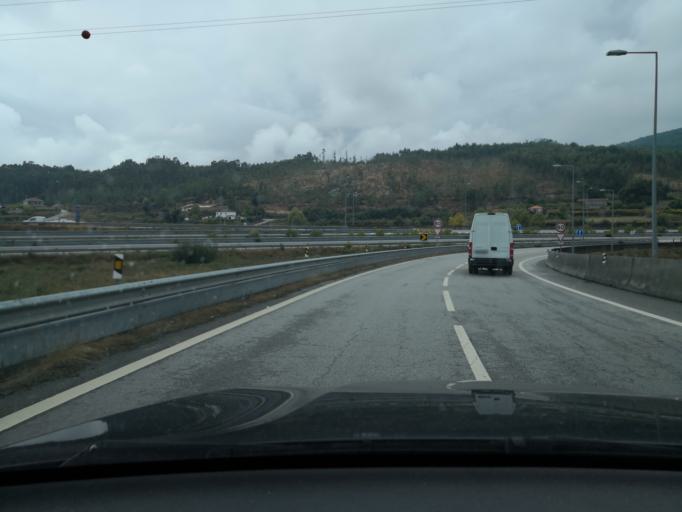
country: PT
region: Porto
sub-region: Lousada
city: Lousada
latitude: 41.2944
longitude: -8.2639
